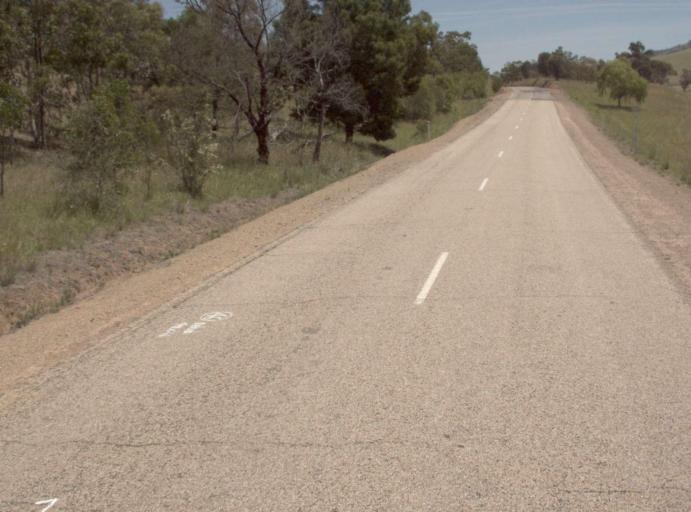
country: AU
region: Victoria
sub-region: East Gippsland
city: Bairnsdale
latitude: -37.3562
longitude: 147.8094
